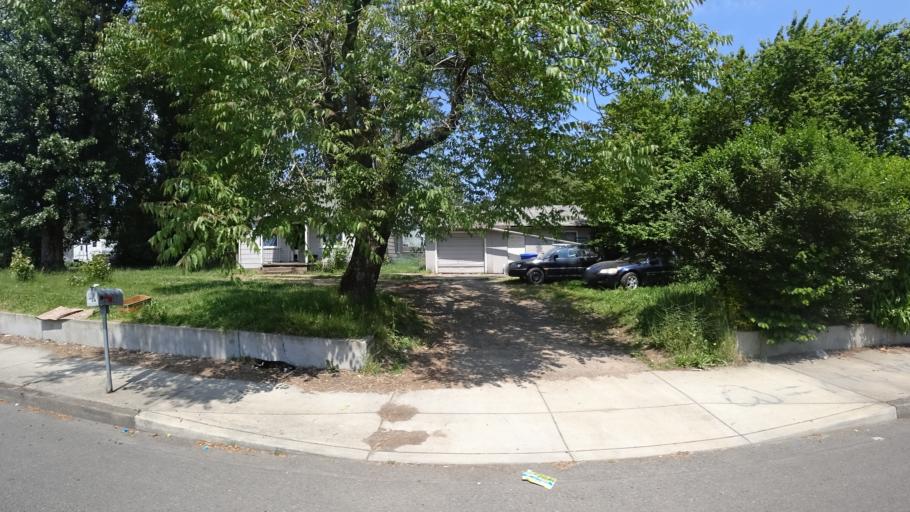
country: US
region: Oregon
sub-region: Multnomah County
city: Fairview
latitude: 45.5265
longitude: -122.5010
